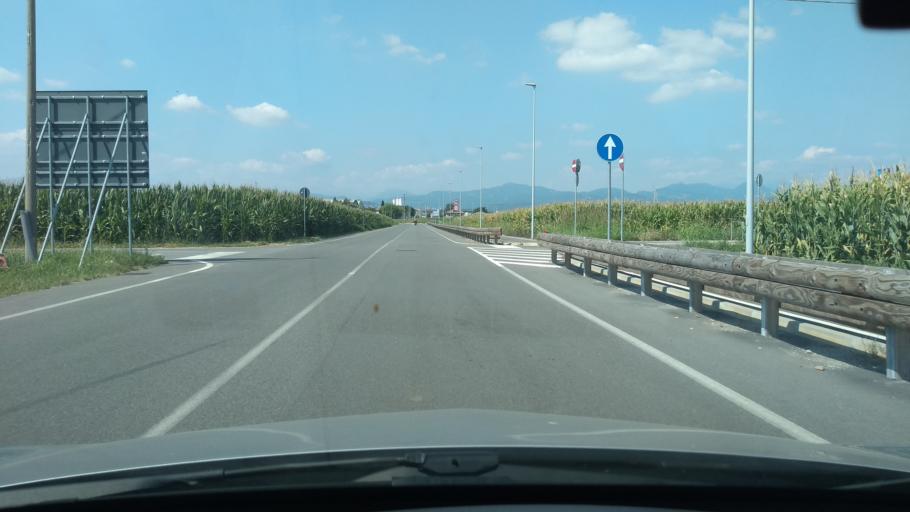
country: IT
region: Lombardy
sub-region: Provincia di Bergamo
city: Zanica
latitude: 45.6375
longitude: 9.6764
